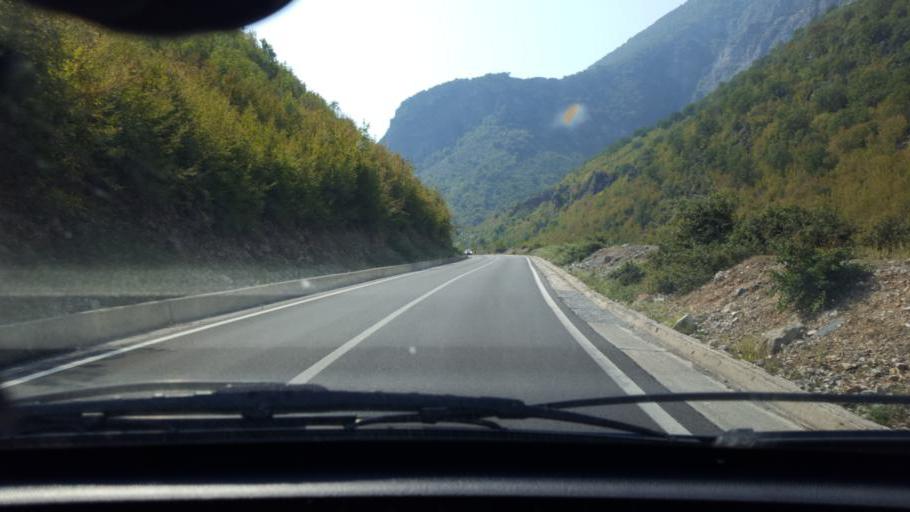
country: AL
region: Shkoder
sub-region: Rrethi i Malesia e Madhe
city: Kastrat
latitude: 42.4473
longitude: 19.5453
